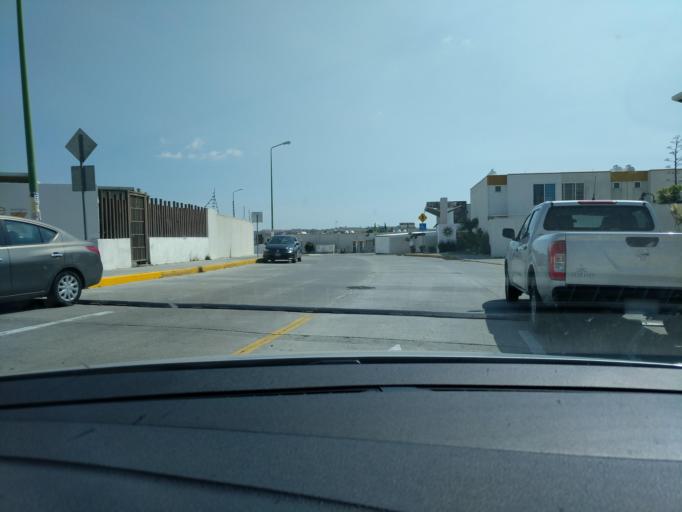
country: MX
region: Puebla
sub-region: Puebla
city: Galaxia la Calera
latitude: 19.0048
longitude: -98.1487
